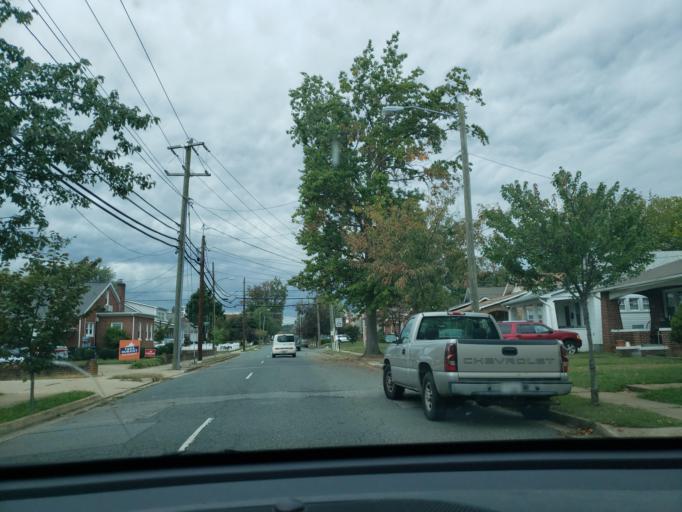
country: US
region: Virginia
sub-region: City of Fredericksburg
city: Fredericksburg
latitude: 38.3105
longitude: -77.4691
